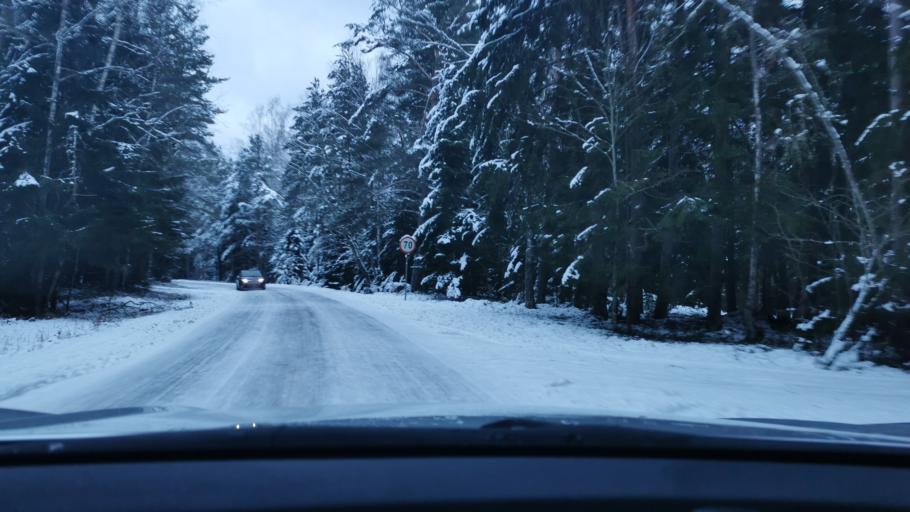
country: EE
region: Laeaene-Virumaa
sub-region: Haljala vald
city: Haljala
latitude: 59.5611
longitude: 26.3135
